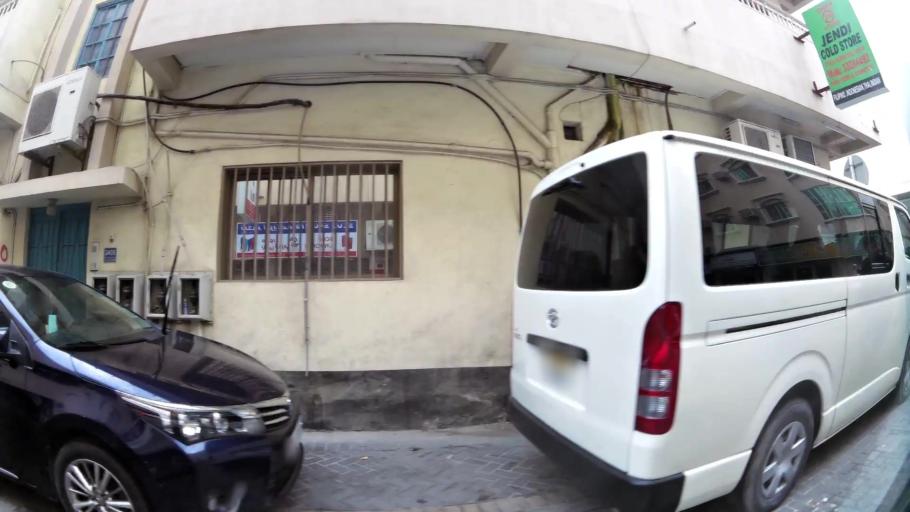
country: BH
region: Manama
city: Manama
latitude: 26.2256
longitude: 50.5887
